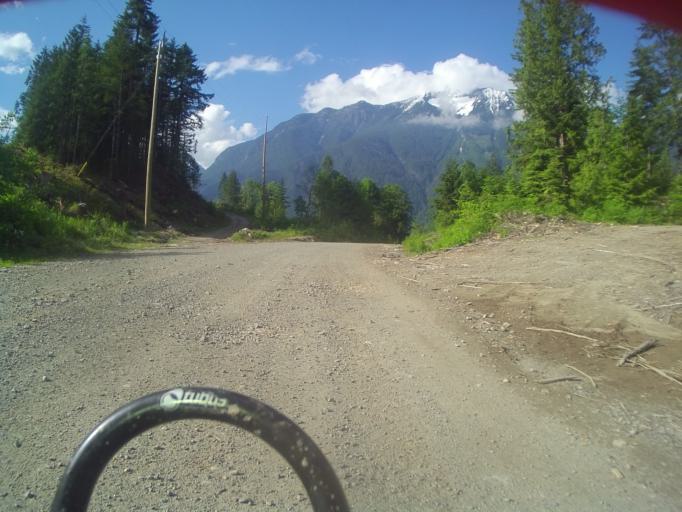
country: CA
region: British Columbia
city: Agassiz
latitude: 49.6613
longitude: -121.9980
